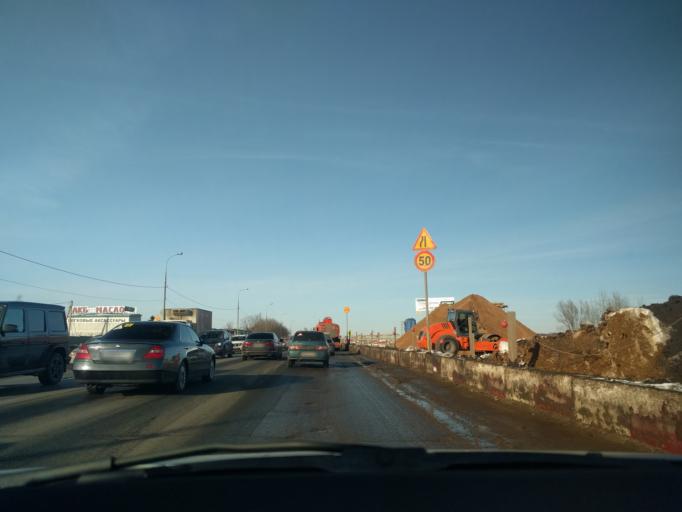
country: RU
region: Moskovskaya
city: Sheremet'yevskiy
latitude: 55.9907
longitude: 37.5322
